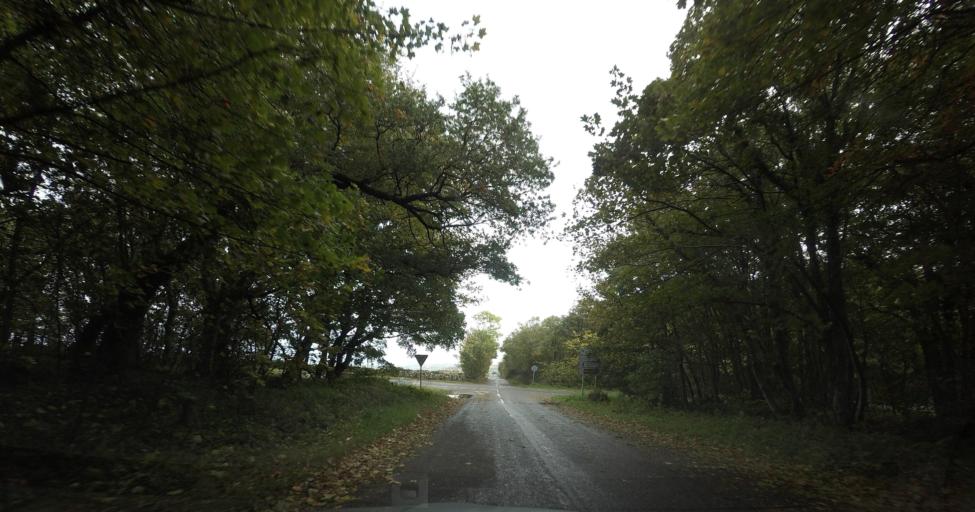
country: GB
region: Scotland
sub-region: Aberdeenshire
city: Whitehills
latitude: 57.6702
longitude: -2.5798
